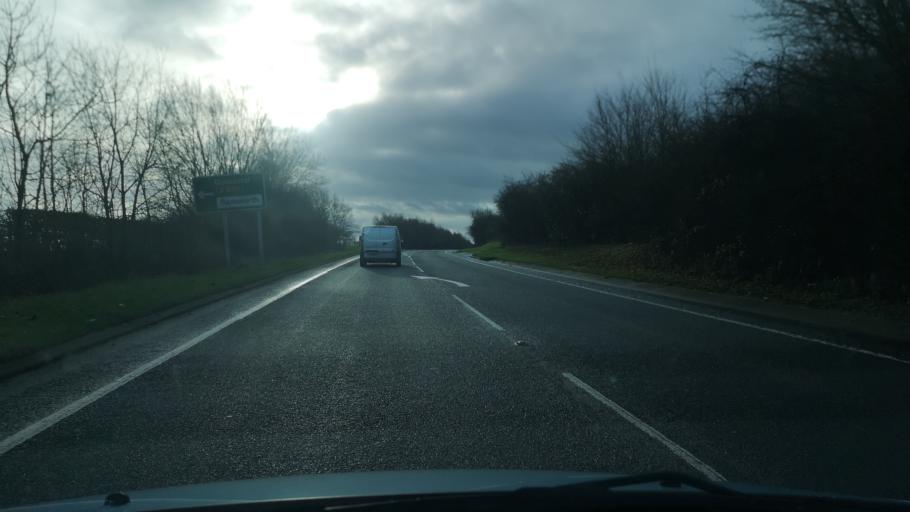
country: GB
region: England
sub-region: City and Borough of Wakefield
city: Hemsworth
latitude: 53.6228
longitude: -1.3345
